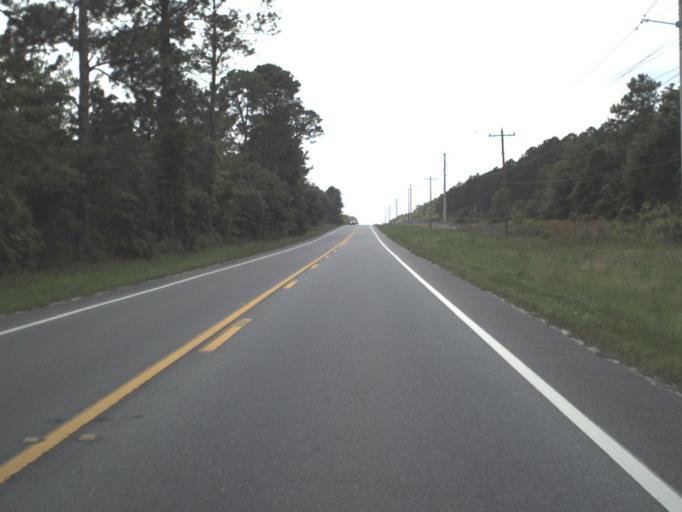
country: US
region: Florida
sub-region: Clay County
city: Keystone Heights
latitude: 29.8749
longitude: -81.9294
